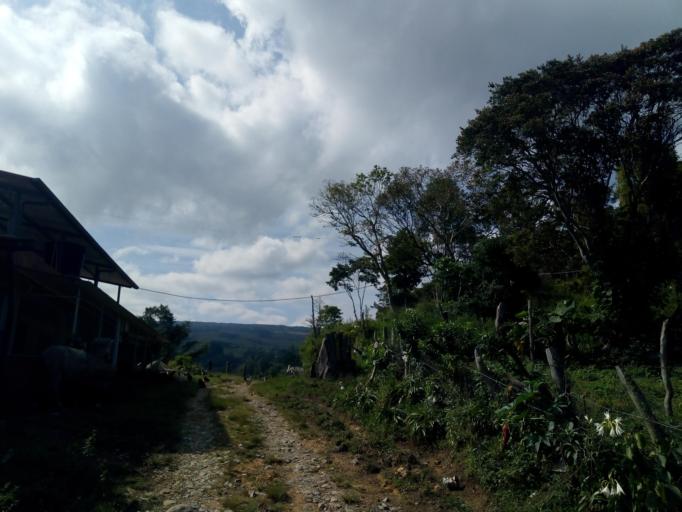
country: CO
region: Boyaca
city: Moniquira
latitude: 5.8738
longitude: -73.5044
